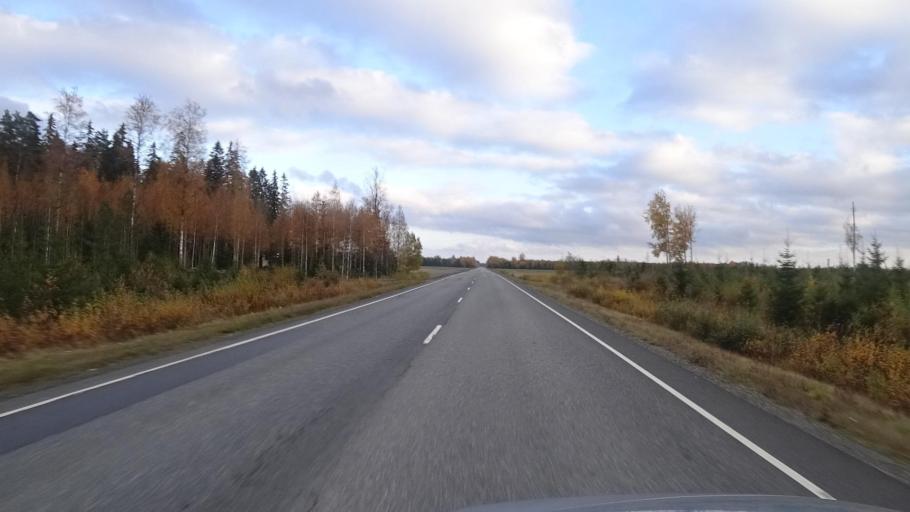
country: FI
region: Varsinais-Suomi
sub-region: Loimaa
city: Alastaro
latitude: 60.9091
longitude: 22.9160
